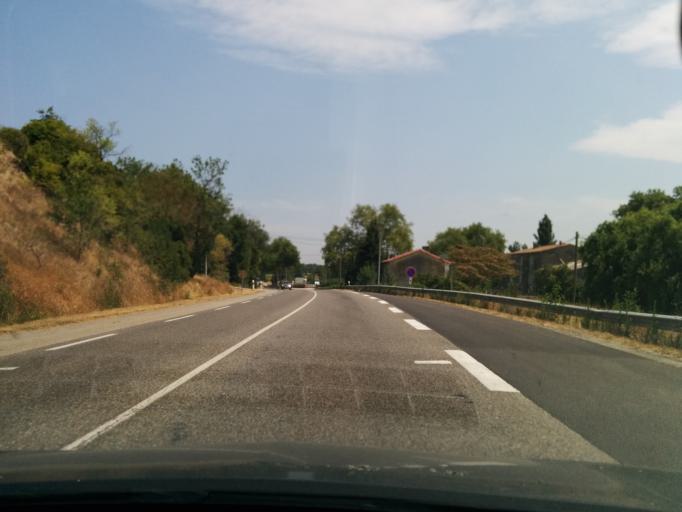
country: FR
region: Languedoc-Roussillon
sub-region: Departement de l'Aude
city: Saint-Martin-Lalande
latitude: 43.2981
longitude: 1.9930
